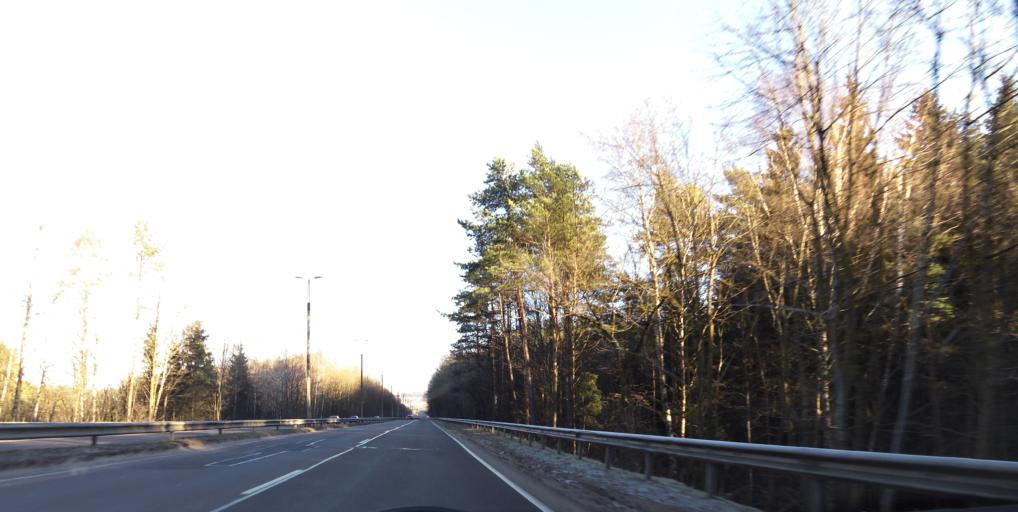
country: LT
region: Vilnius County
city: Lazdynai
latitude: 54.6396
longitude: 25.1928
